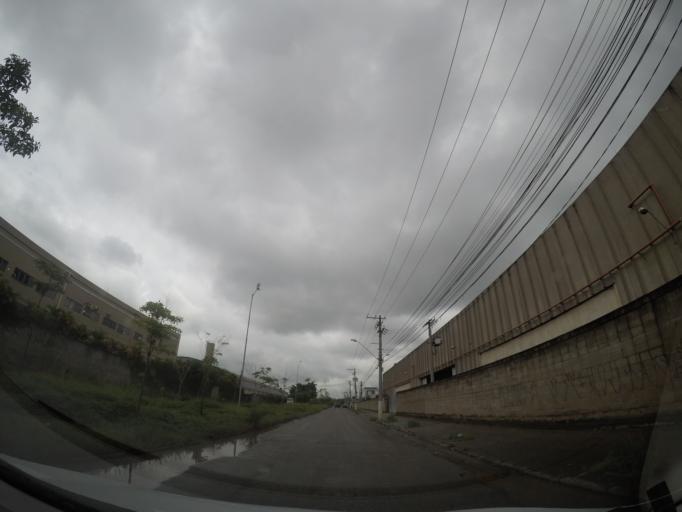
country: BR
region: Sao Paulo
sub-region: Guarulhos
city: Guarulhos
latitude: -23.4714
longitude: -46.4793
